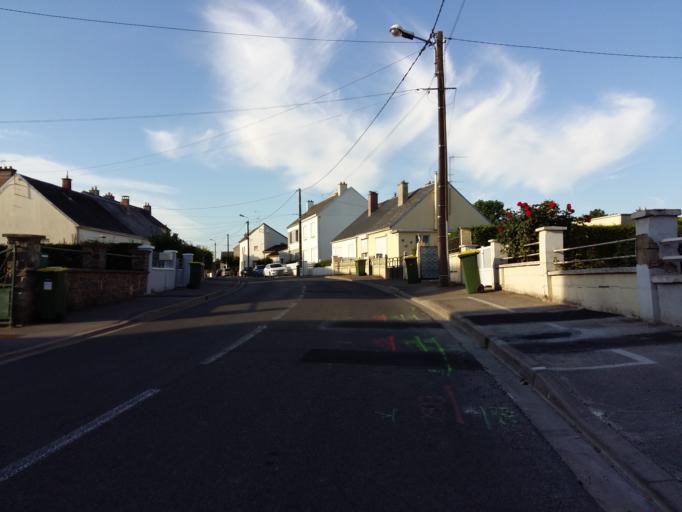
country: FR
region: Picardie
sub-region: Departement de la Somme
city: Rivery
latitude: 49.9005
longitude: 2.3316
